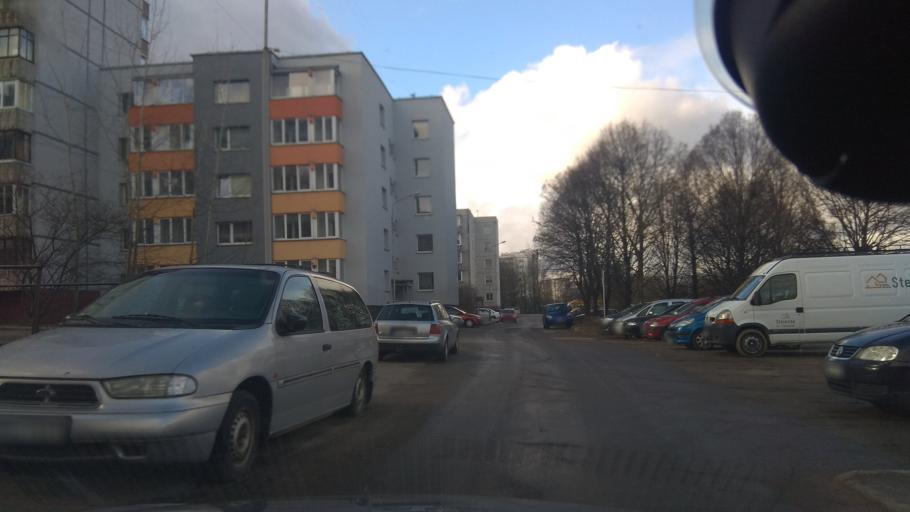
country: LT
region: Vilnius County
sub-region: Vilnius
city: Fabijoniskes
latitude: 54.7196
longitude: 25.2407
